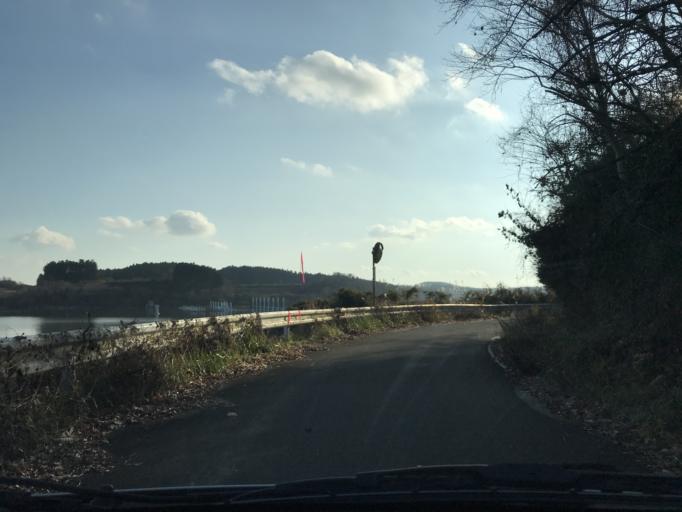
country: JP
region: Miyagi
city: Wakuya
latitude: 38.6925
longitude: 141.1114
